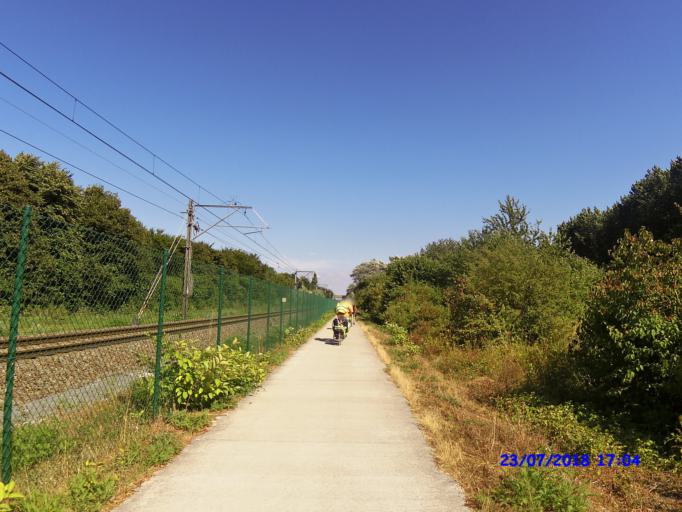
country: BE
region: Flanders
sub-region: Provincie West-Vlaanderen
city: Veurne
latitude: 51.0719
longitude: 2.6831
